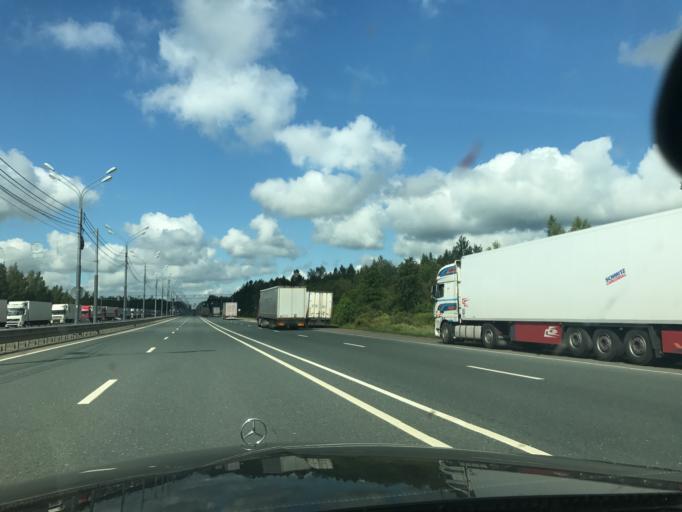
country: RU
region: Smolensk
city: Rudnya
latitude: 54.6912
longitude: 31.0137
